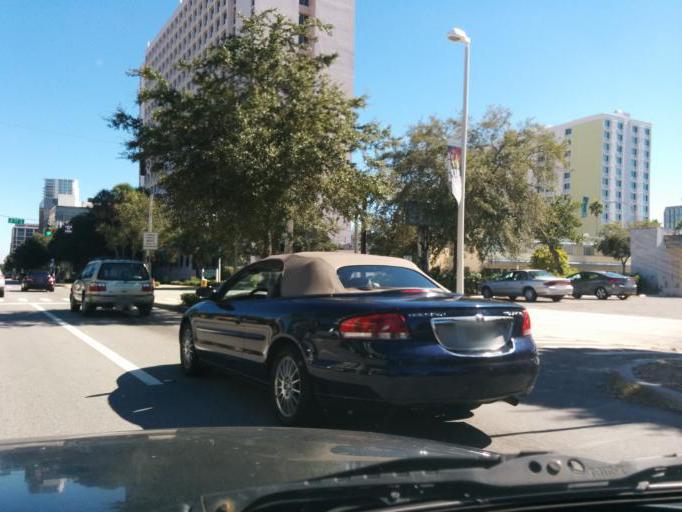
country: US
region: Florida
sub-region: Pinellas County
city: Saint Petersburg
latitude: 27.7703
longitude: -82.6422
